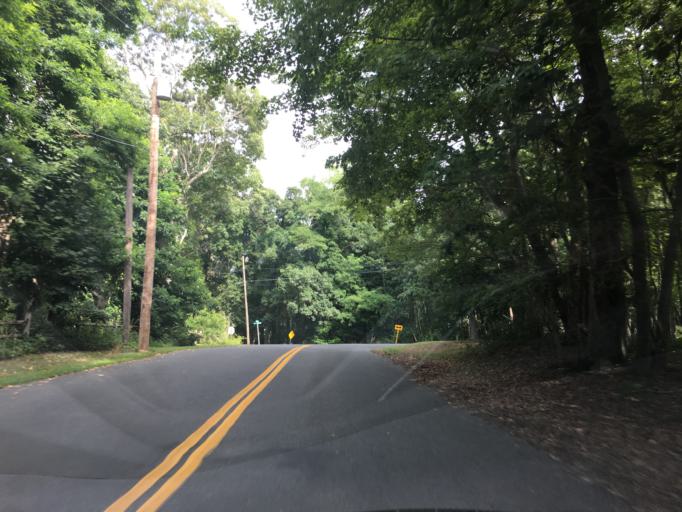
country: US
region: New York
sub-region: Suffolk County
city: Shelter Island Heights
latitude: 41.0693
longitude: -72.3813
